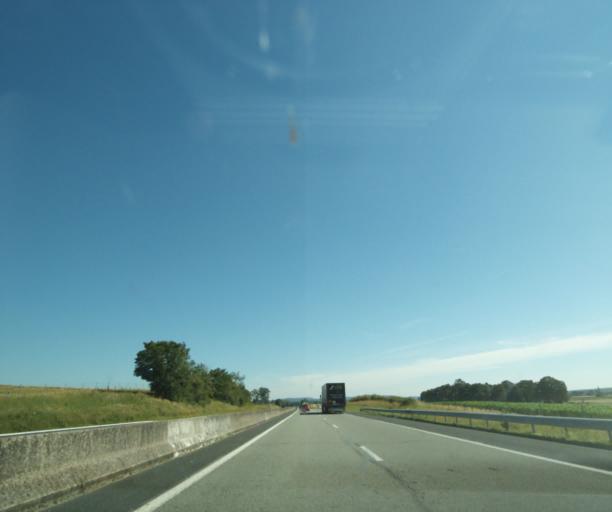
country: FR
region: Lorraine
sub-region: Departement des Vosges
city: Lamarche
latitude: 48.1160
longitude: 5.6609
